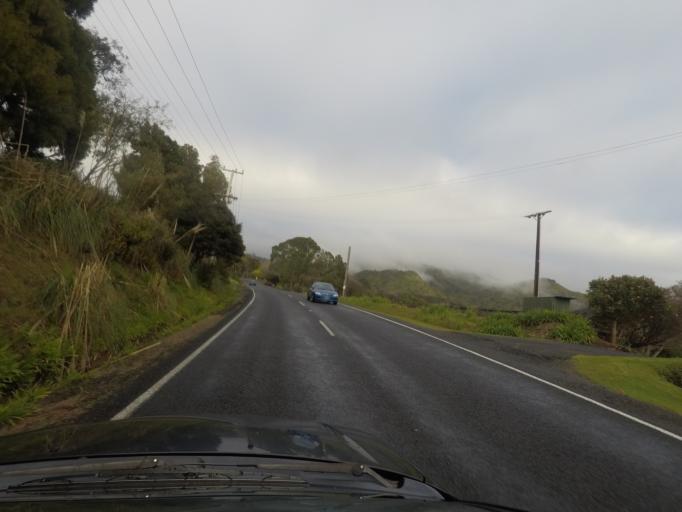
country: NZ
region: Auckland
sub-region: Auckland
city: Waitakere
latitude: -36.9187
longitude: 174.5870
